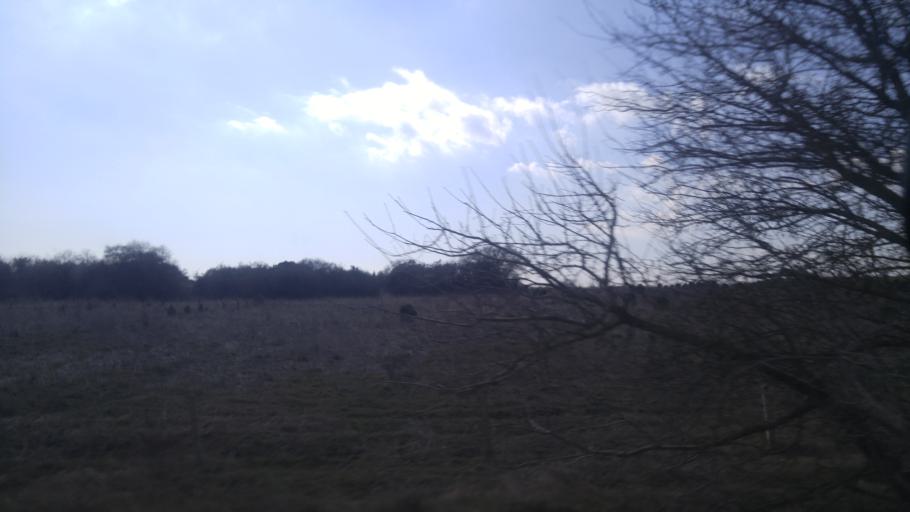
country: TR
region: Istanbul
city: Canta
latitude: 41.1715
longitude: 28.0936
